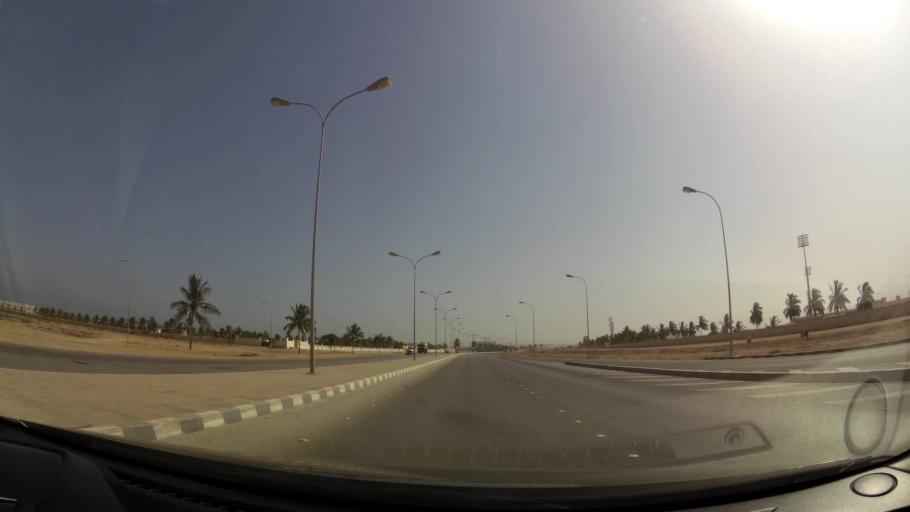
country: OM
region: Zufar
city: Salalah
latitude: 16.9924
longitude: 54.0278
